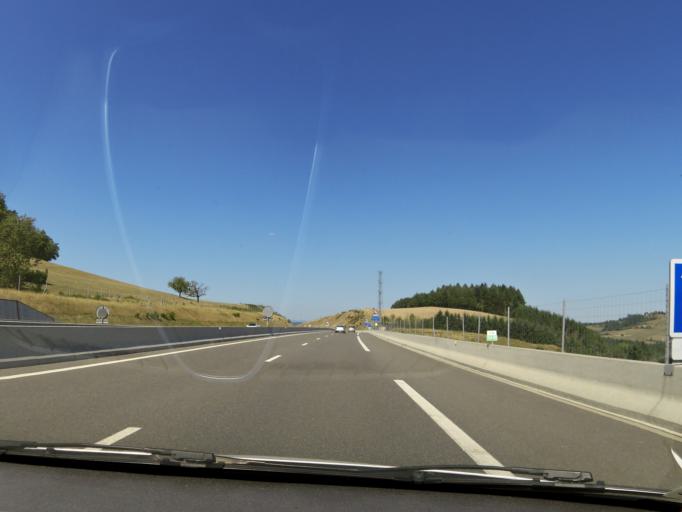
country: FR
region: Rhone-Alpes
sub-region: Departement de la Loire
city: Bussieres
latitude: 45.8675
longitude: 4.3017
